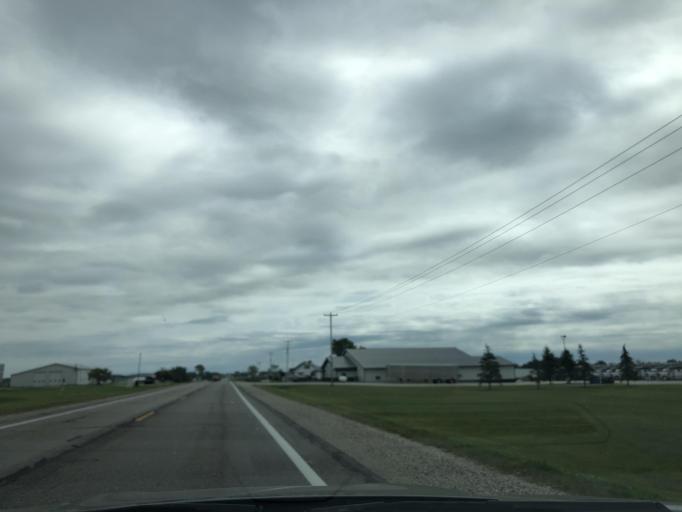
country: US
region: Michigan
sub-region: Missaukee County
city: Lake City
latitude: 44.1936
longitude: -85.1710
